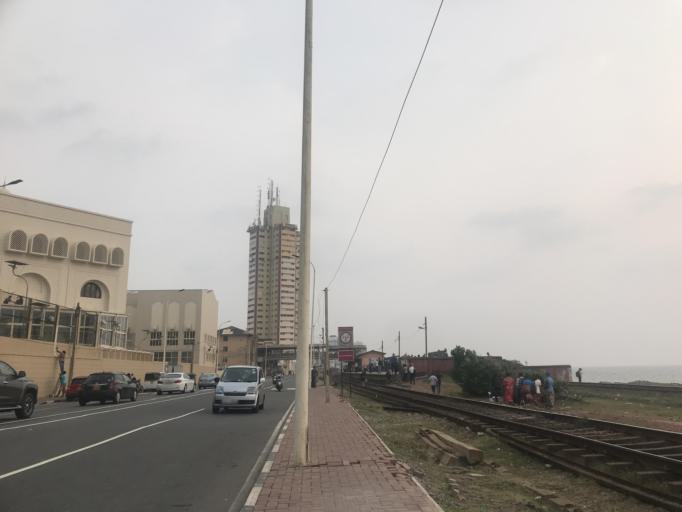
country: LK
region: Western
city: Colombo
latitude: 6.8950
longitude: 79.8526
